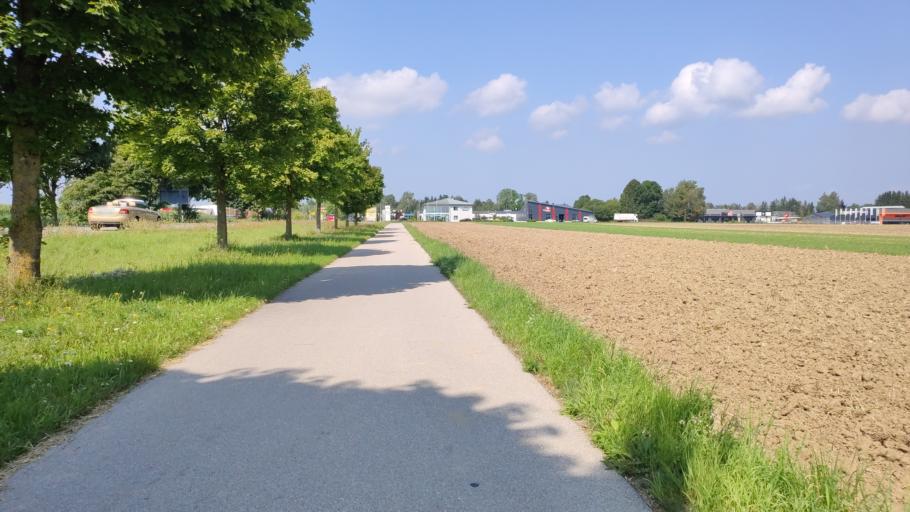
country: DE
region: Bavaria
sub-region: Swabia
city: Bobingen
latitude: 48.2625
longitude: 10.8451
